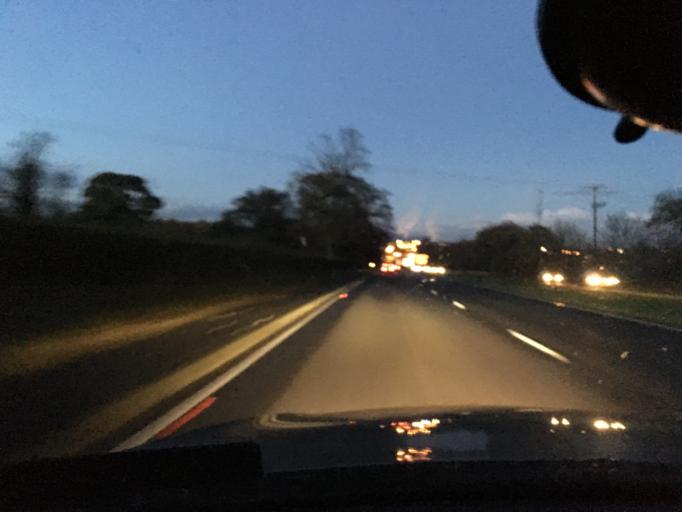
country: GB
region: Northern Ireland
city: Hillsborough
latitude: 54.4817
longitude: -6.0692
